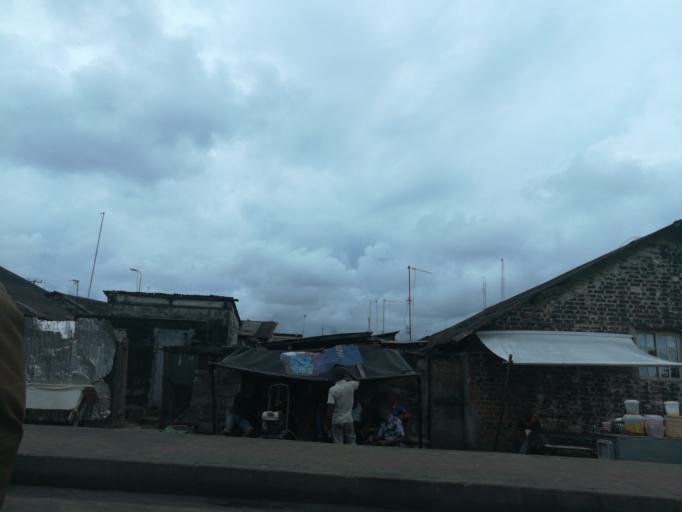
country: NG
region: Rivers
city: Port Harcourt
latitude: 4.7631
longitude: 7.0189
